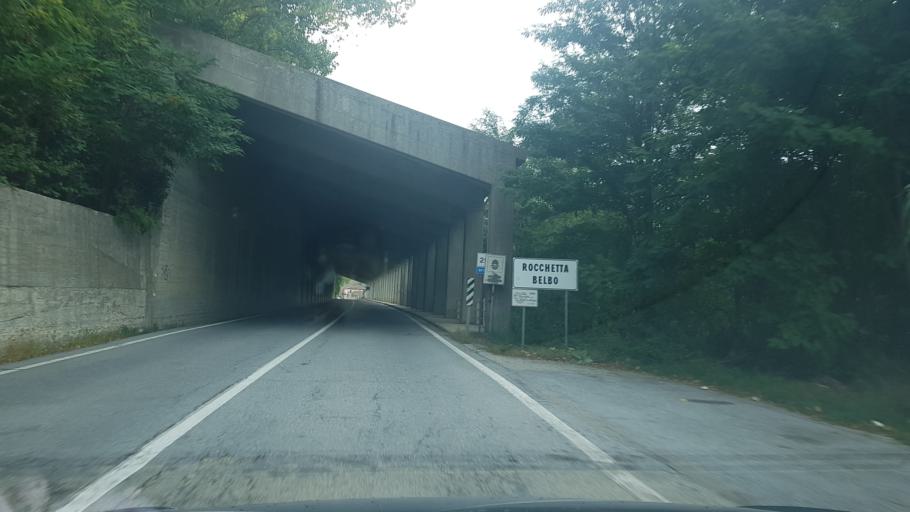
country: IT
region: Piedmont
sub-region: Provincia di Cuneo
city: Rocchetta Belbo
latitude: 44.6331
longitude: 8.1701
